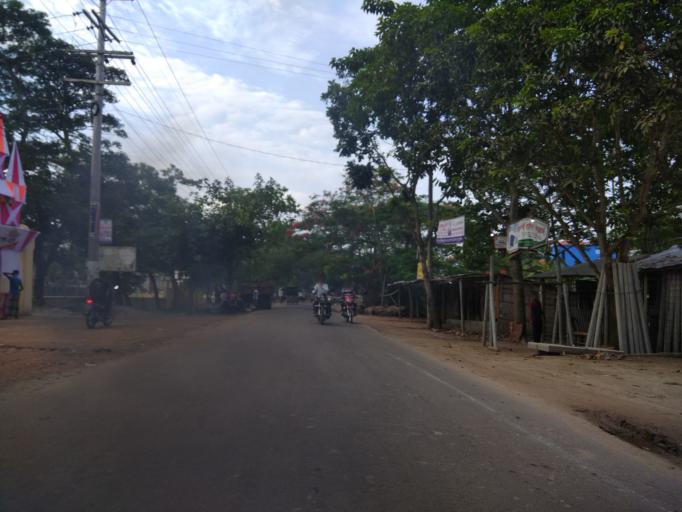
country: IN
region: West Bengal
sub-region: North 24 Parganas
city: Taki
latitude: 22.3403
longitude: 89.1057
